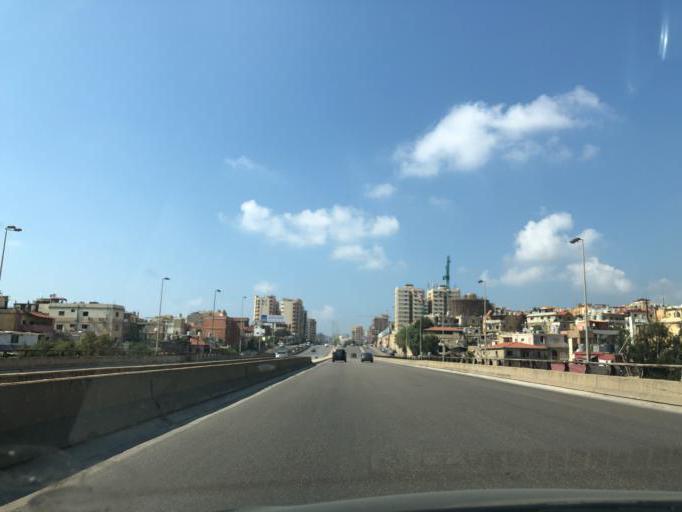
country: LB
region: Beyrouth
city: Beirut
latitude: 33.8601
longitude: 35.4858
